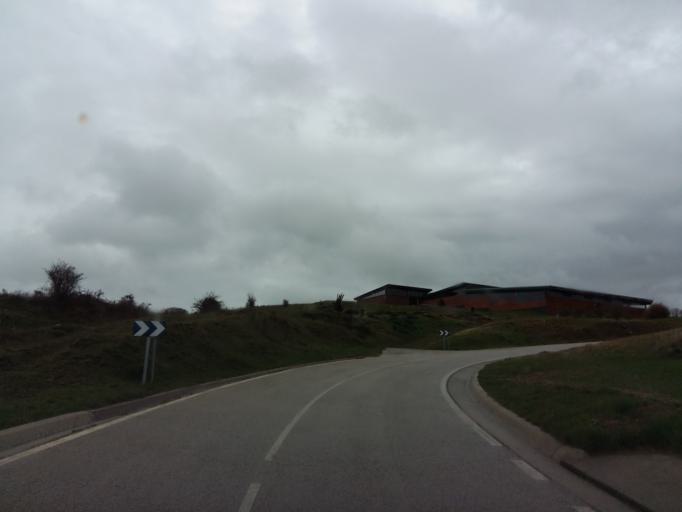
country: ES
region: Cantabria
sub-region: Provincia de Cantabria
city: Mataporquera
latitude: 42.8862
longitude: -4.1589
